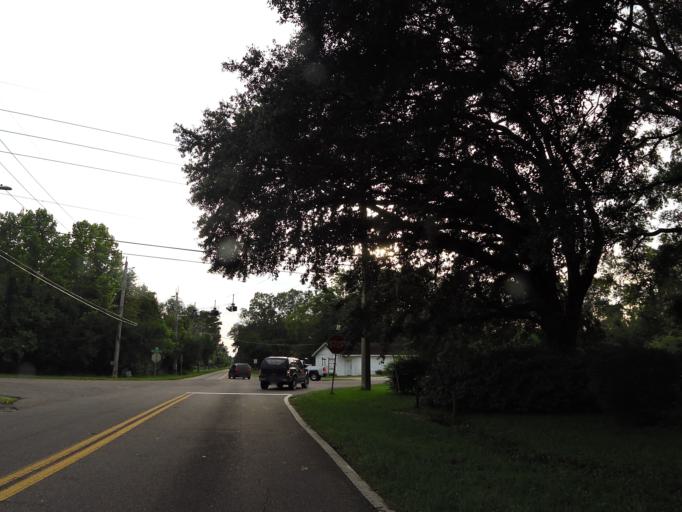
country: US
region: Florida
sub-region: Nassau County
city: Nassau Village-Ratliff
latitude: 30.4158
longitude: -81.7598
